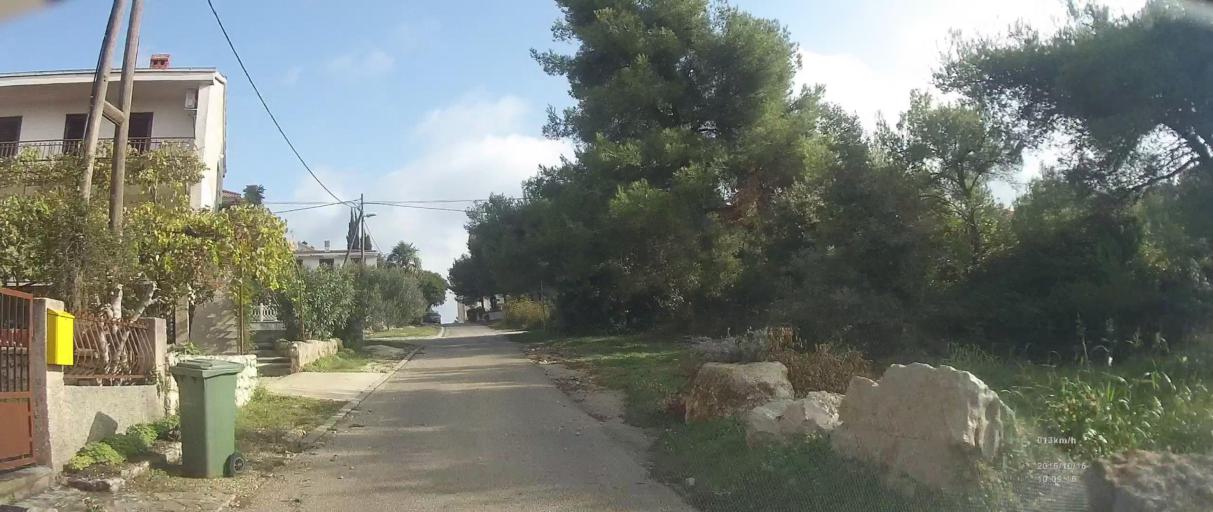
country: HR
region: Zadarska
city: Pakostane
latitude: 43.9130
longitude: 15.5058
